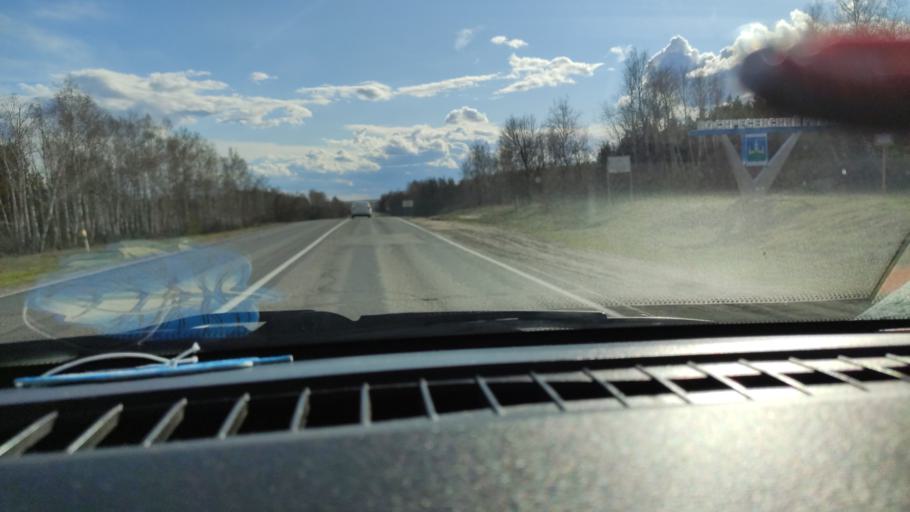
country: RU
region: Saratov
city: Sennoy
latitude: 52.1152
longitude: 46.8366
